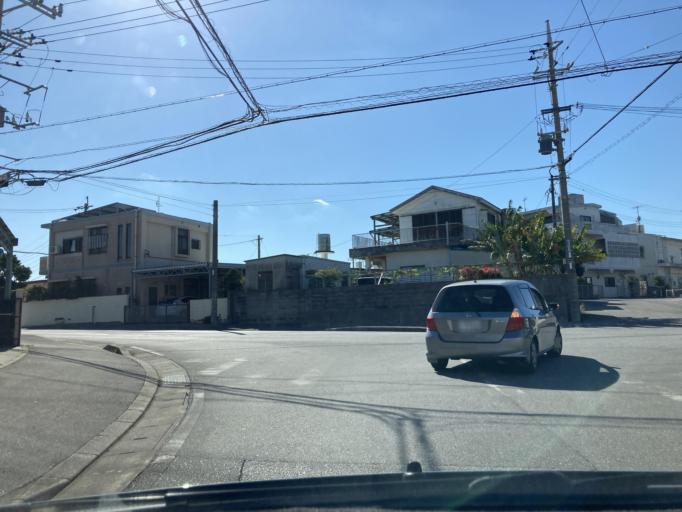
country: JP
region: Okinawa
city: Okinawa
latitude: 26.3623
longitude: 127.8246
